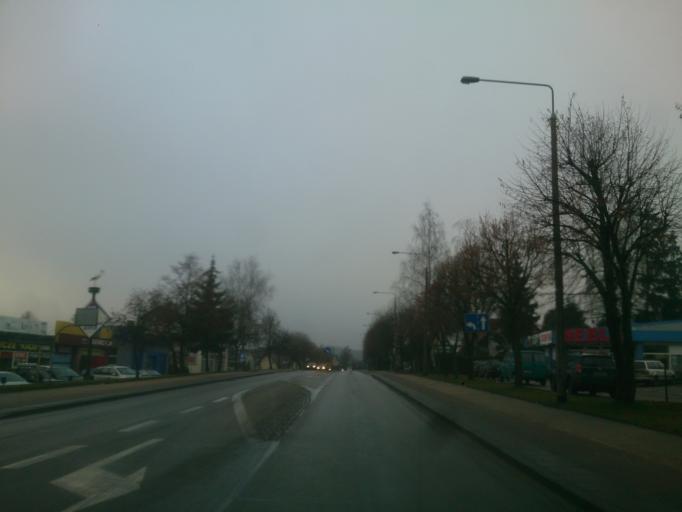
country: PL
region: Pomeranian Voivodeship
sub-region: Powiat koscierski
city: Koscierzyna
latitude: 54.1180
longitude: 17.9747
